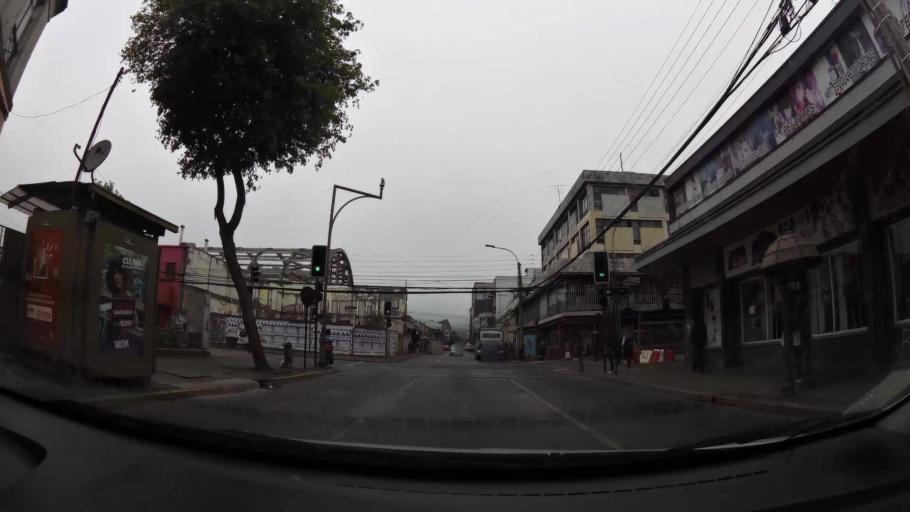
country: CL
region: Biobio
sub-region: Provincia de Concepcion
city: Concepcion
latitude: -36.8251
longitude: -73.0539
